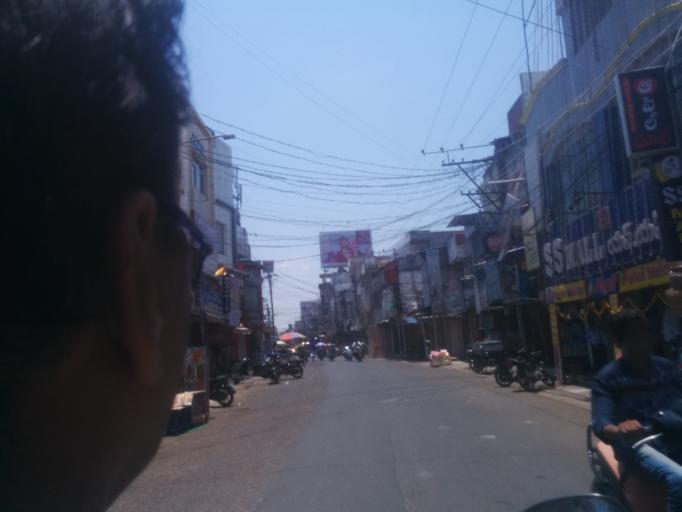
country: IN
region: Andhra Pradesh
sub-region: East Godavari
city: Rajahmundry
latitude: 17.0044
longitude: 81.7703
